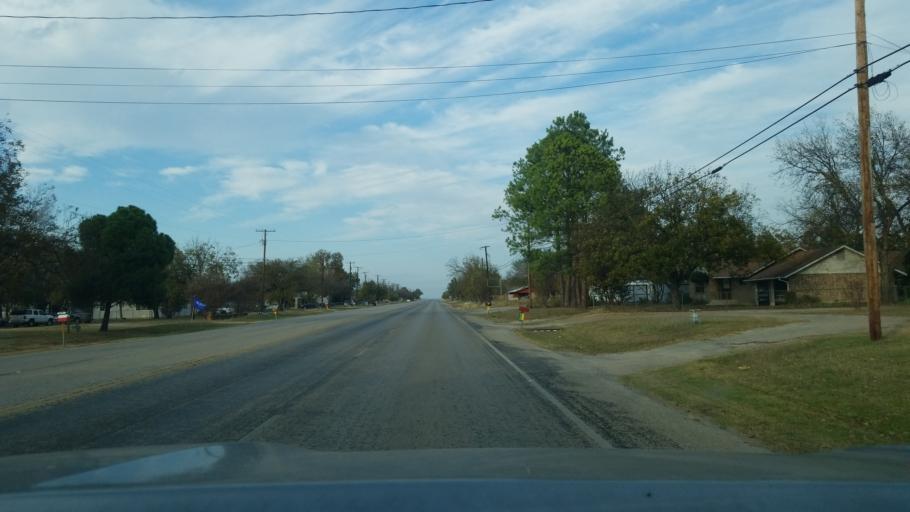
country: US
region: Texas
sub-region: Brown County
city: Early
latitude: 31.7642
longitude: -98.9559
